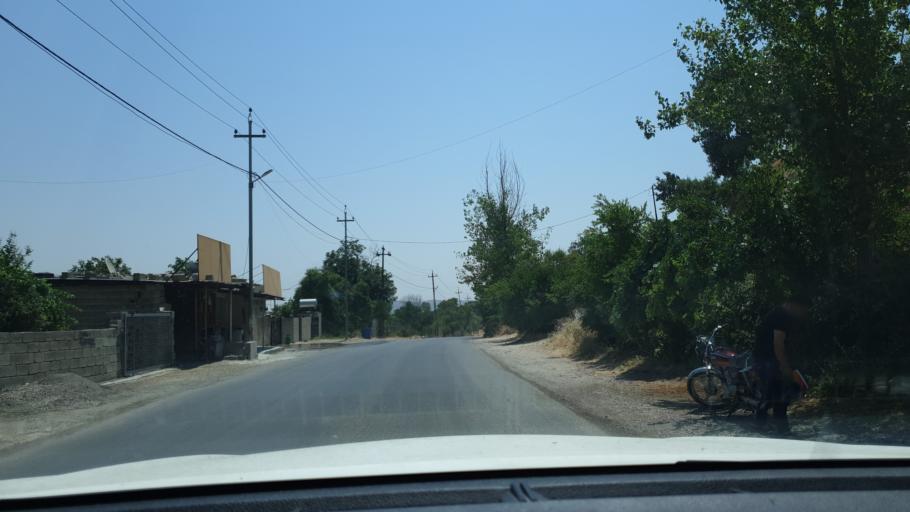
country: IQ
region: Arbil
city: Nahiyat Hiran
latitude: 36.2857
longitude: 44.4874
